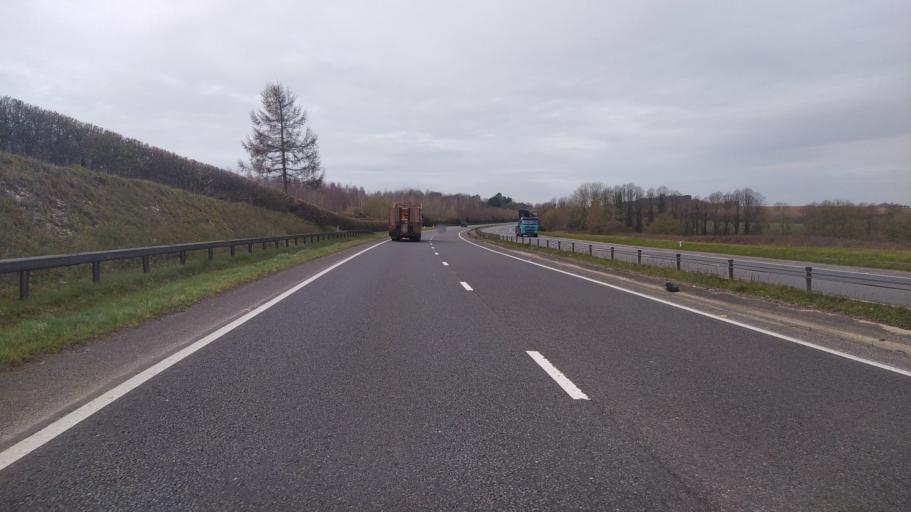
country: GB
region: England
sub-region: Dorset
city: Bovington Camp
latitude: 50.7526
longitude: -2.2514
